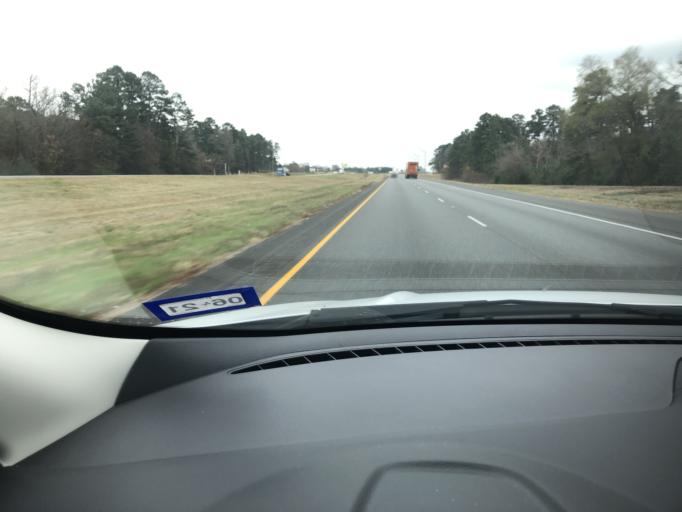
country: US
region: Texas
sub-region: Angelina County
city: Redland
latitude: 31.4190
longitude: -94.7231
